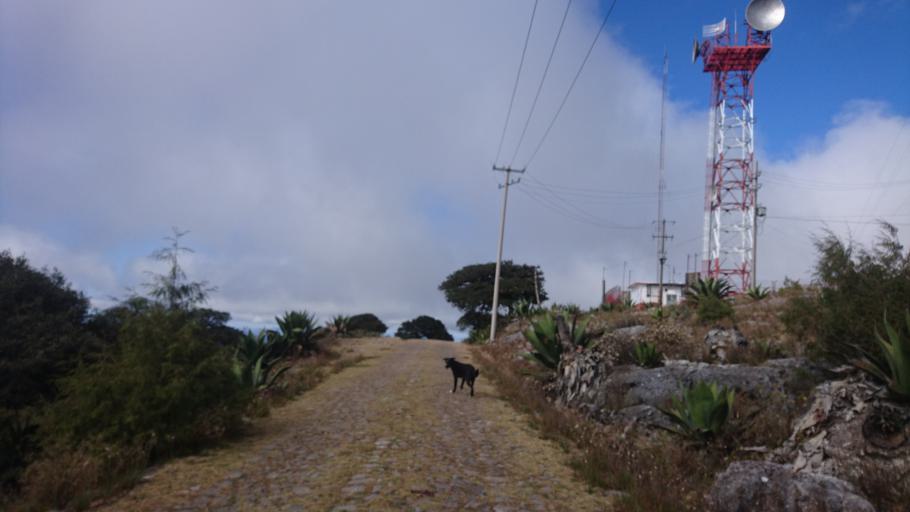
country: MX
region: San Luis Potosi
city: Zaragoza
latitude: 22.0672
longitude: -100.6472
